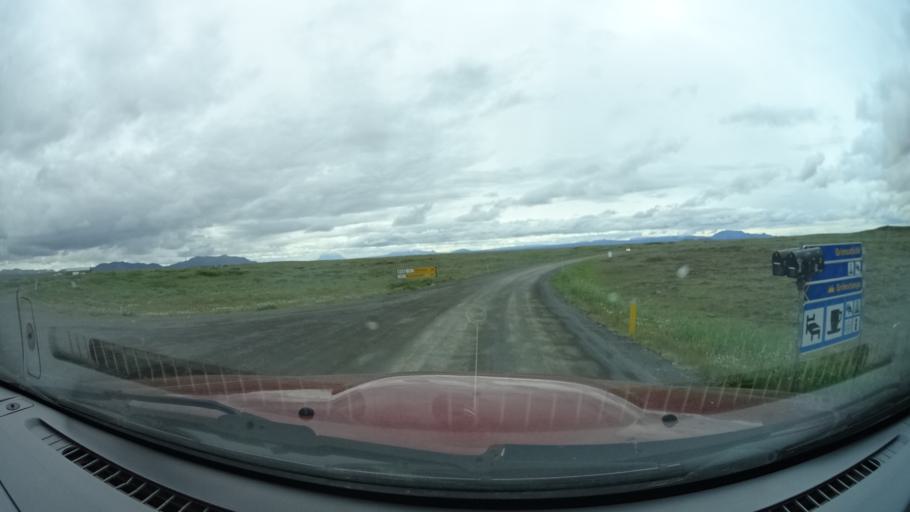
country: IS
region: Northeast
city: Laugar
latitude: 65.6451
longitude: -16.1295
